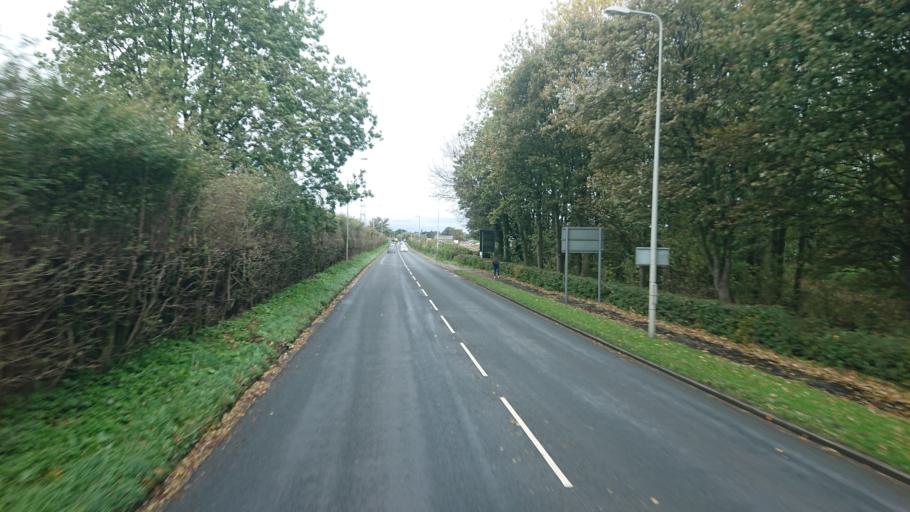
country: GB
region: England
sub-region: Lancashire
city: Galgate
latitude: 54.0138
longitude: -2.7954
